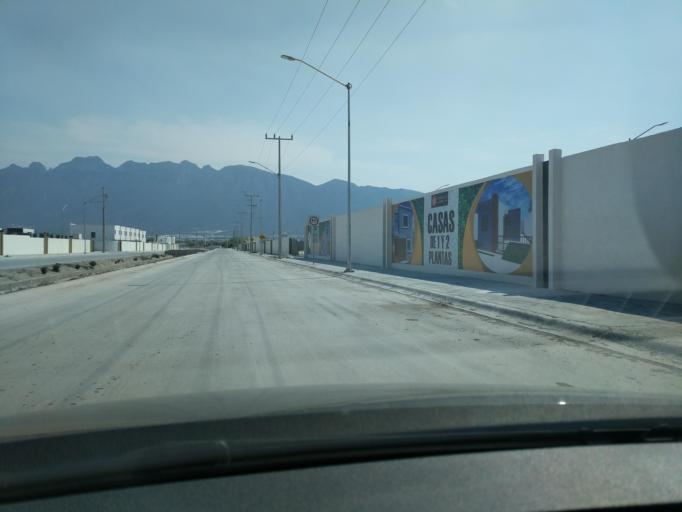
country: MX
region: Nuevo Leon
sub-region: Garcia
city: Valle de Lincoln
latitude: 25.7967
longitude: -100.4716
